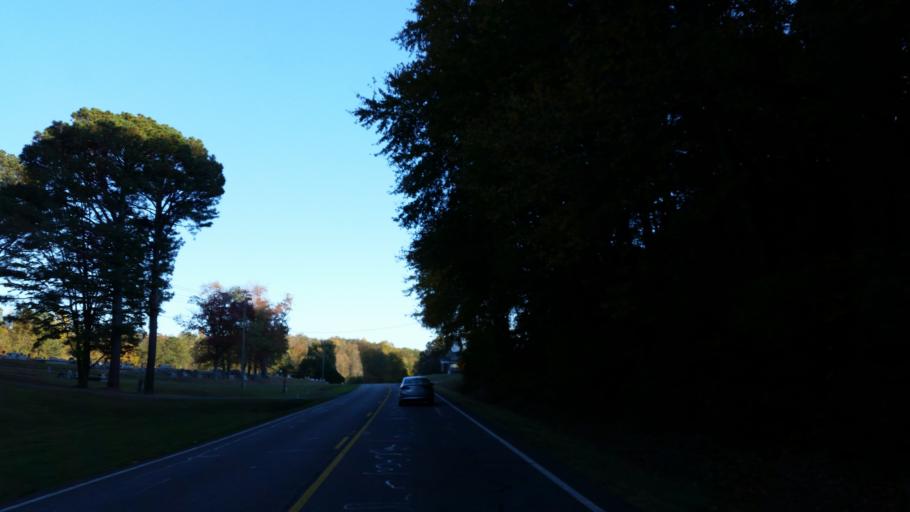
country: US
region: Georgia
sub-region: Gilmer County
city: Ellijay
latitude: 34.6156
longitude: -84.3638
